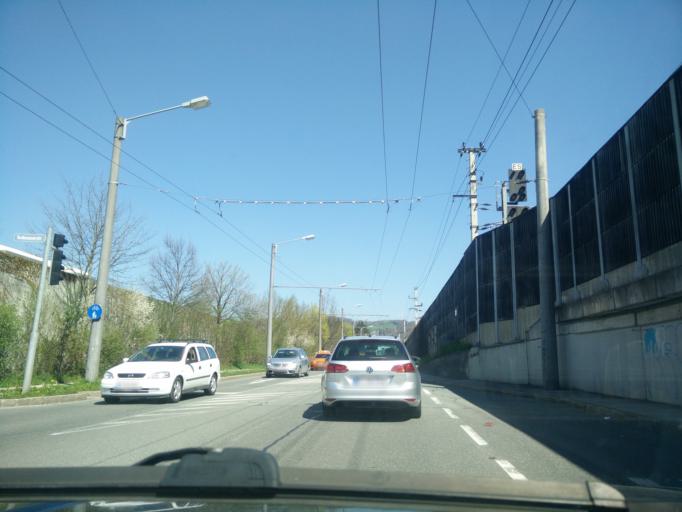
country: AT
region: Salzburg
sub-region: Politischer Bezirk Salzburg-Umgebung
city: Elsbethen
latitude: 47.7794
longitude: 13.0813
